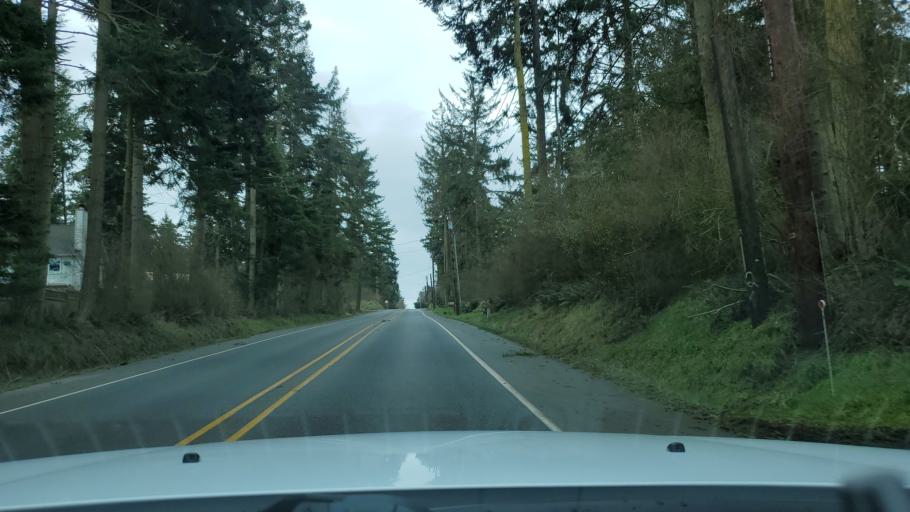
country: US
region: Washington
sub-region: Island County
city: Ault Field
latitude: 48.2930
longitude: -122.7255
